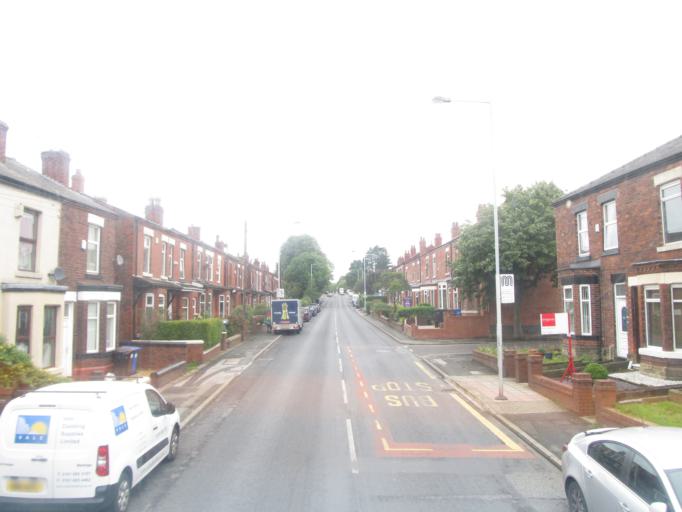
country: GB
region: England
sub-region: Borough of Tameside
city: Haughton Green
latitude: 53.4305
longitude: -2.0911
